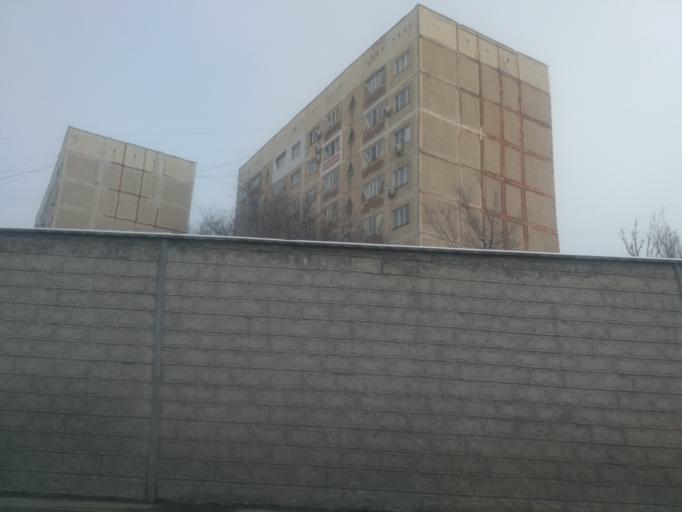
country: KZ
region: Almaty Qalasy
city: Almaty
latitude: 43.1949
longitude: 76.8775
